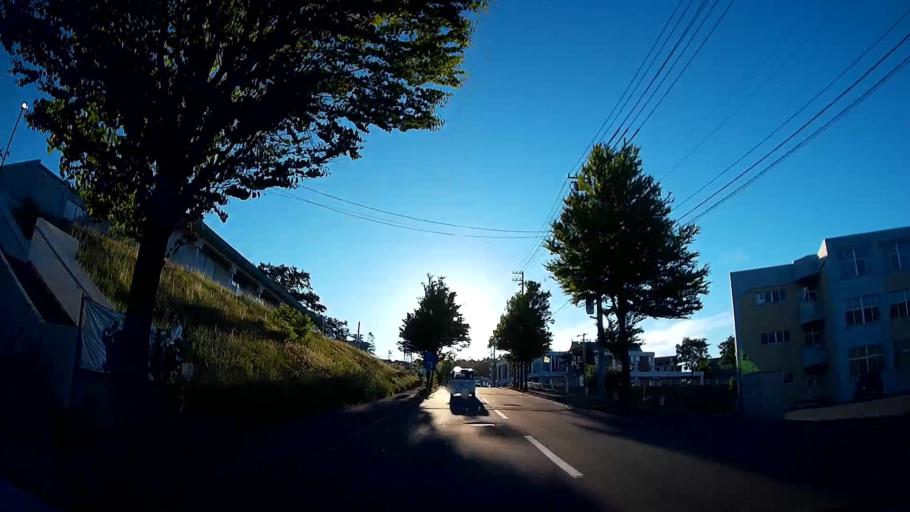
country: JP
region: Hokkaido
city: Otaru
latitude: 43.1658
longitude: 141.0399
